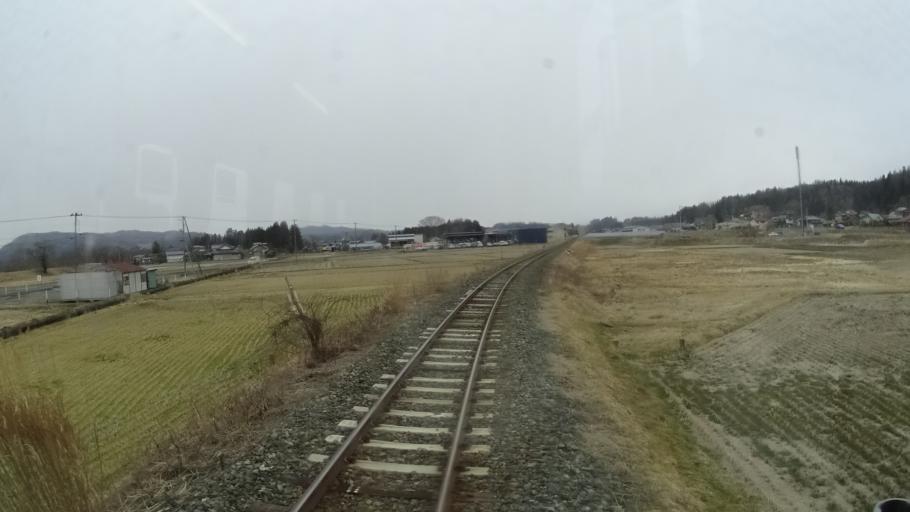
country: JP
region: Iwate
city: Hanamaki
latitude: 39.3781
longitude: 141.2408
